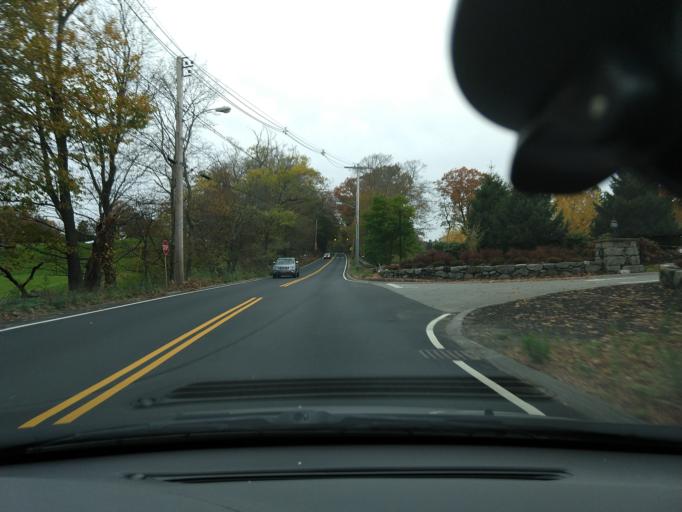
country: US
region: Massachusetts
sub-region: Middlesex County
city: Belmont
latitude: 42.4102
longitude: -71.2013
